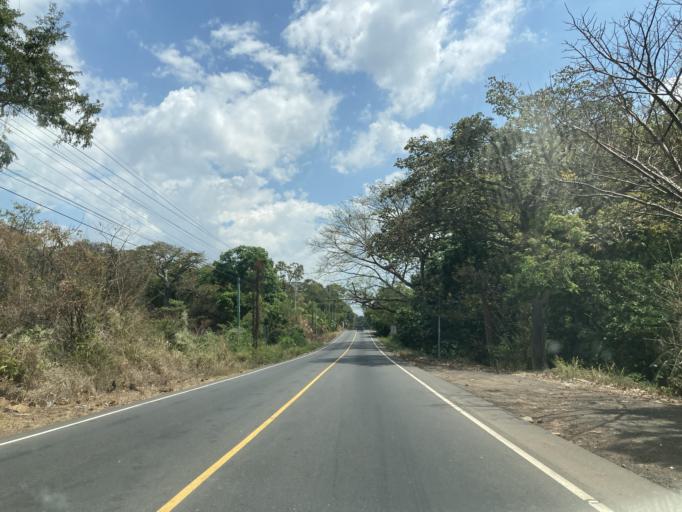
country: GT
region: Santa Rosa
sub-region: Municipio de Taxisco
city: Taxisco
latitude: 14.0672
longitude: -90.4422
